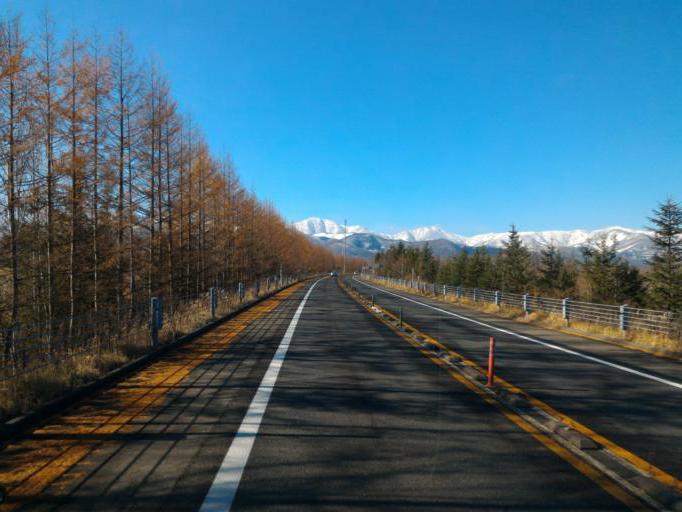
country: JP
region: Hokkaido
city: Otofuke
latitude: 42.9714
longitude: 142.8994
